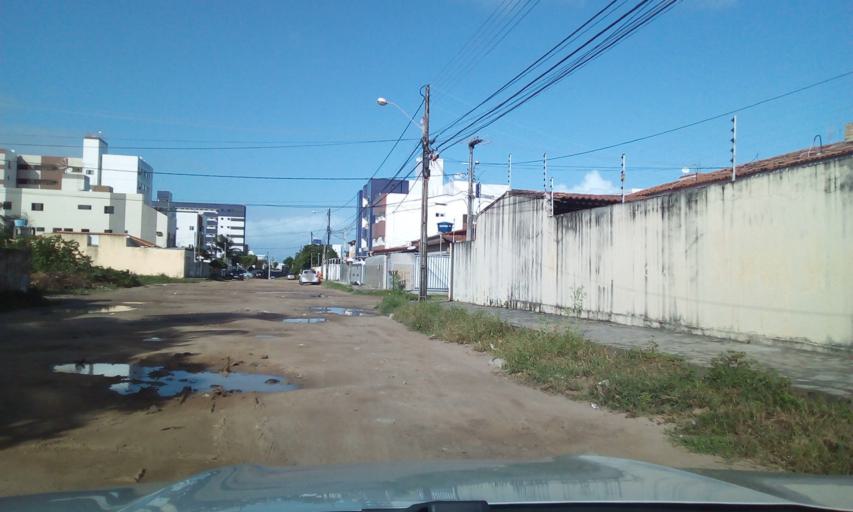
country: BR
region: Paraiba
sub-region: Joao Pessoa
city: Joao Pessoa
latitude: -7.1582
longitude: -34.8335
